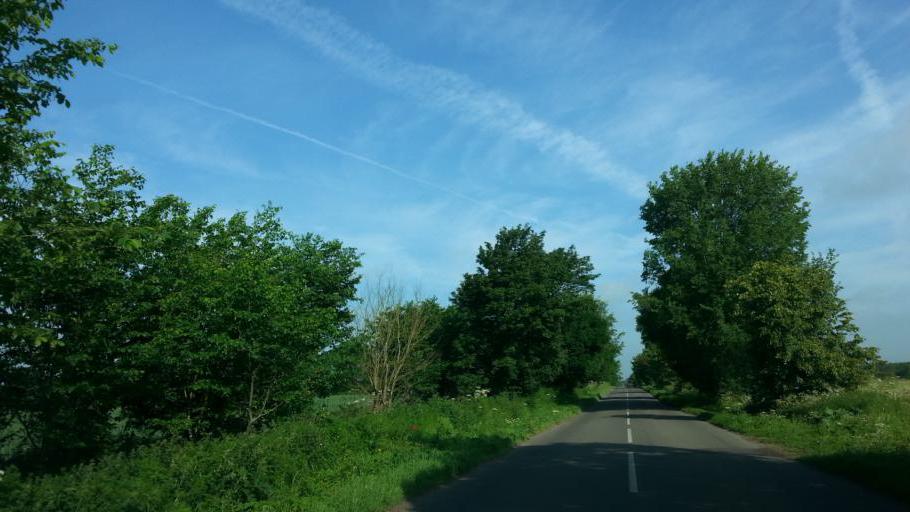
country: GB
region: England
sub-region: Nottinghamshire
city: Farndon
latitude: 53.0498
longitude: -0.8359
